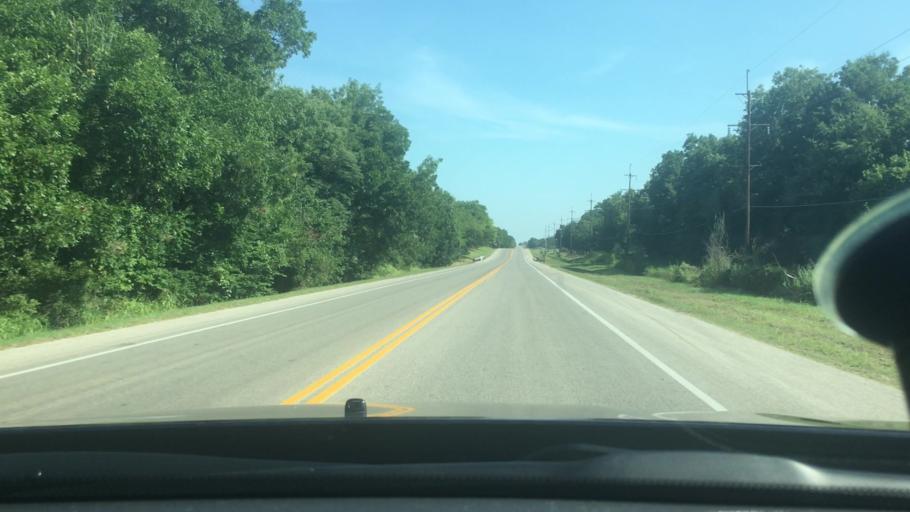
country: US
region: Oklahoma
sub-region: Garvin County
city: Pauls Valley
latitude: 34.6860
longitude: -97.2129
